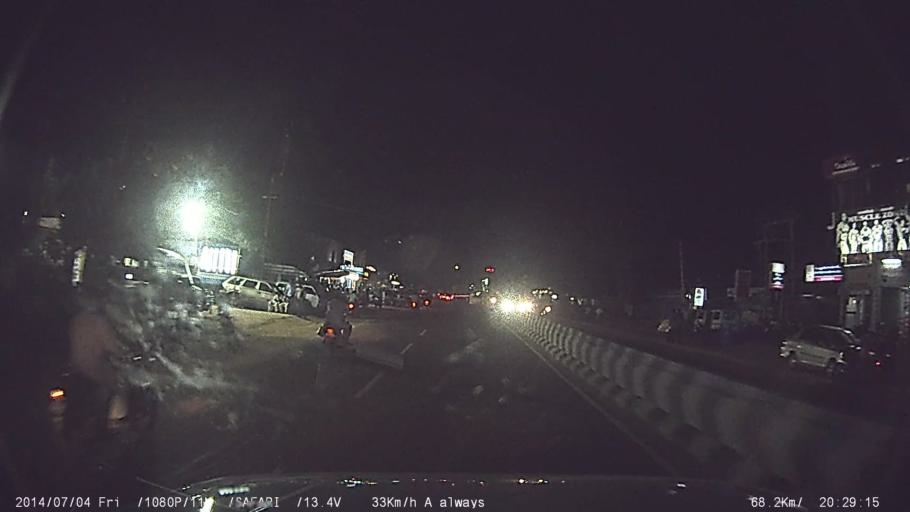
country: IN
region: Tamil Nadu
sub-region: Coimbatore
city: Perur
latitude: 10.9560
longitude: 76.9538
